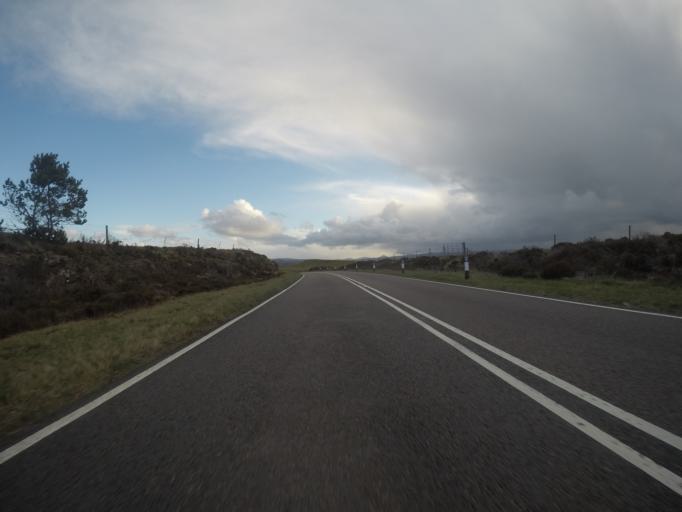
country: GB
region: Scotland
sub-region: Highland
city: Portree
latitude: 57.5468
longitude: -6.3646
